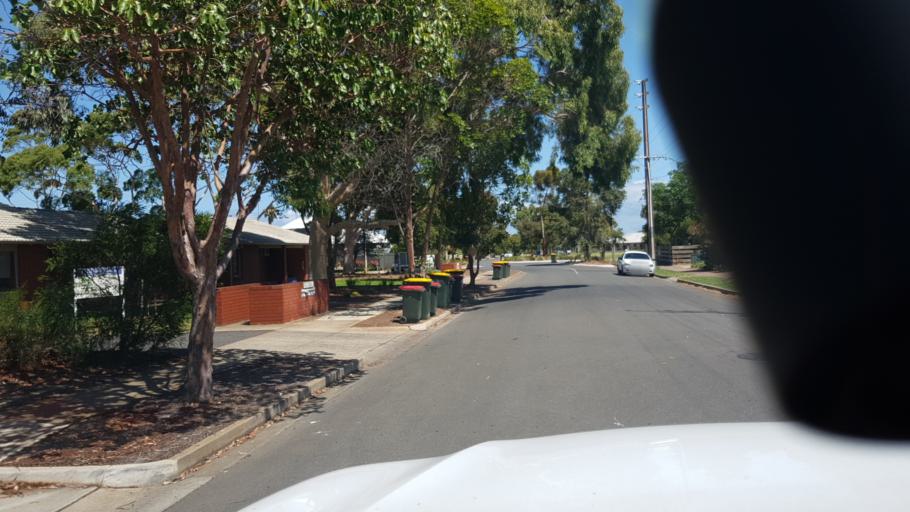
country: AU
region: South Australia
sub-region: Holdfast Bay
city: North Brighton
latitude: -35.0077
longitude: 138.5289
